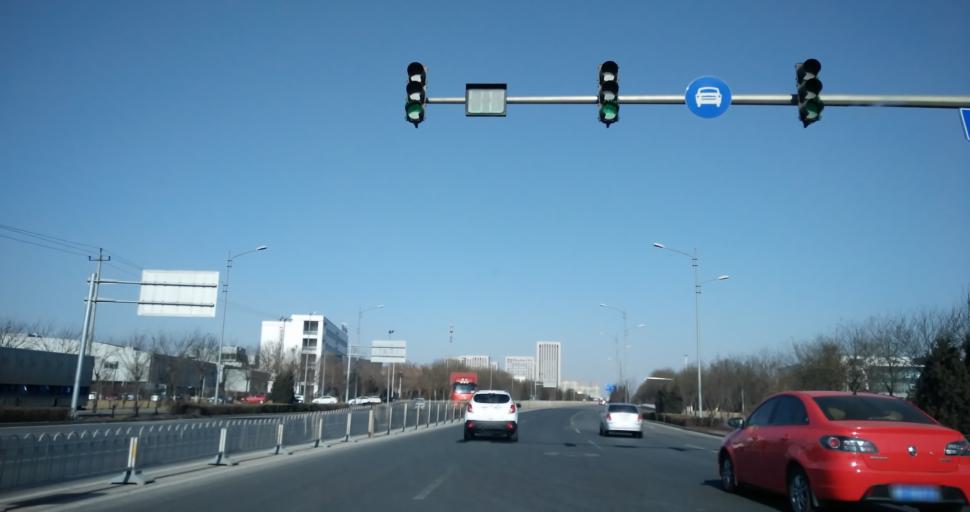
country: CN
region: Beijing
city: Qingyundian
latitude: 39.7392
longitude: 116.4957
